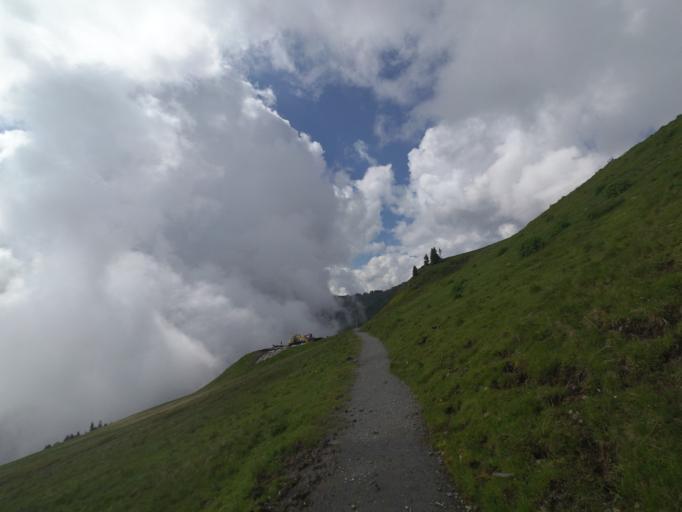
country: AT
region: Salzburg
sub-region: Politischer Bezirk Zell am See
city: Viehhofen
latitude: 47.4069
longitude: 12.7105
